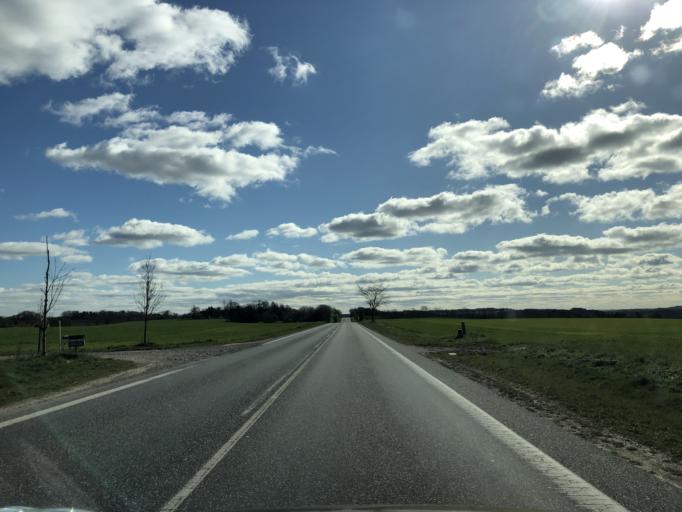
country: DK
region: North Denmark
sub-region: Vesthimmerland Kommune
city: Alestrup
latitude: 56.6145
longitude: 9.6274
